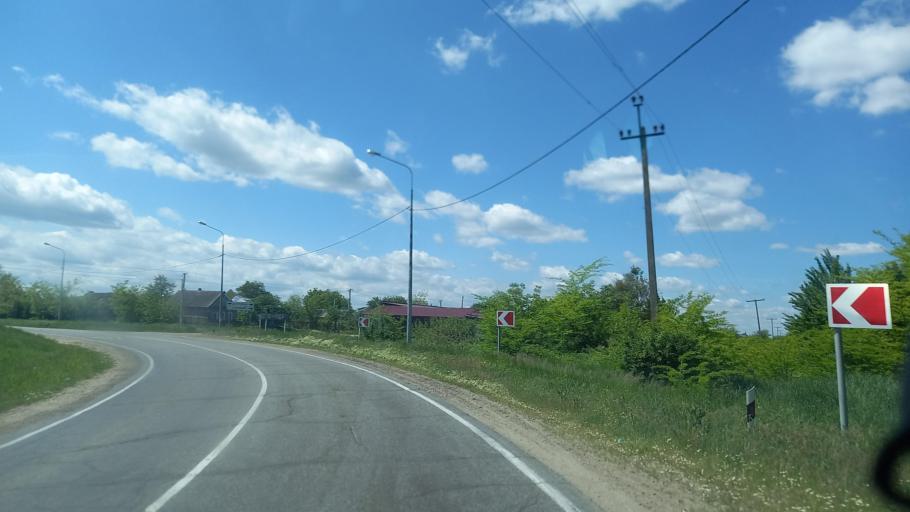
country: RU
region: Krasnodarskiy
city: Tbilisskaya
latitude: 45.3352
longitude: 40.2977
